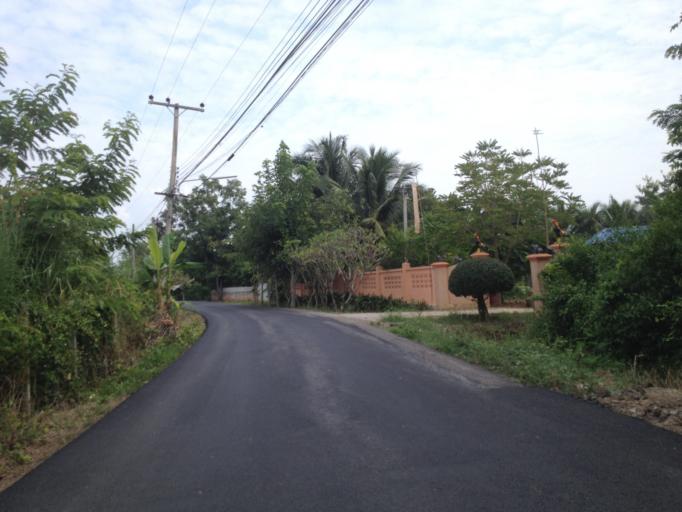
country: TH
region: Chiang Mai
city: Hang Dong
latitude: 18.6755
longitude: 98.9050
